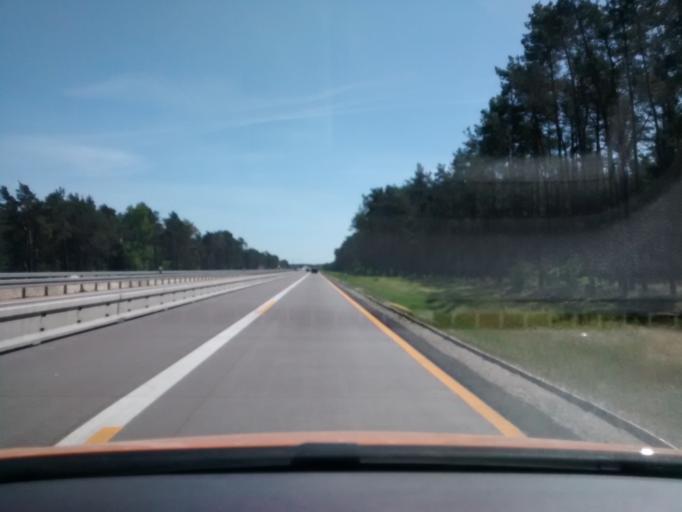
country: DE
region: Brandenburg
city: Spreenhagen
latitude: 52.3151
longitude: 13.8012
